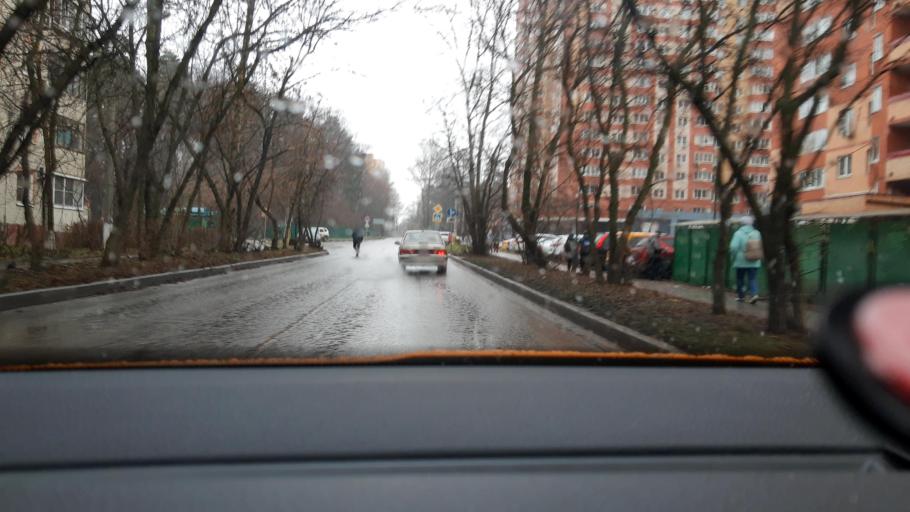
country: RU
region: Moskovskaya
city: Yubileyny
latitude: 55.9294
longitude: 37.8438
